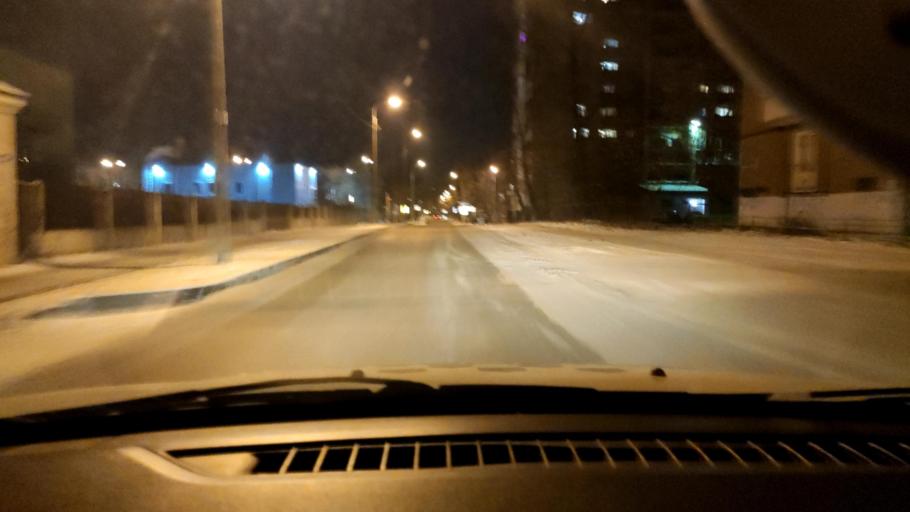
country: RU
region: Perm
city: Kultayevo
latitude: 58.0088
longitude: 55.9542
